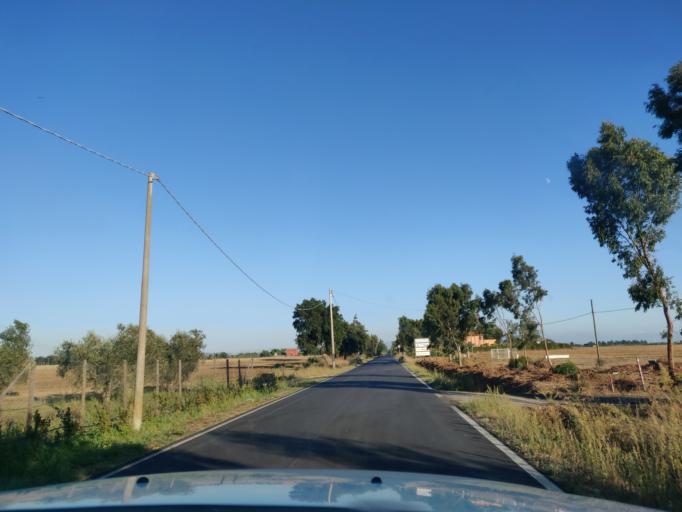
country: IT
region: Latium
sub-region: Provincia di Viterbo
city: Montalto di Castro
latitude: 42.2922
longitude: 11.6556
